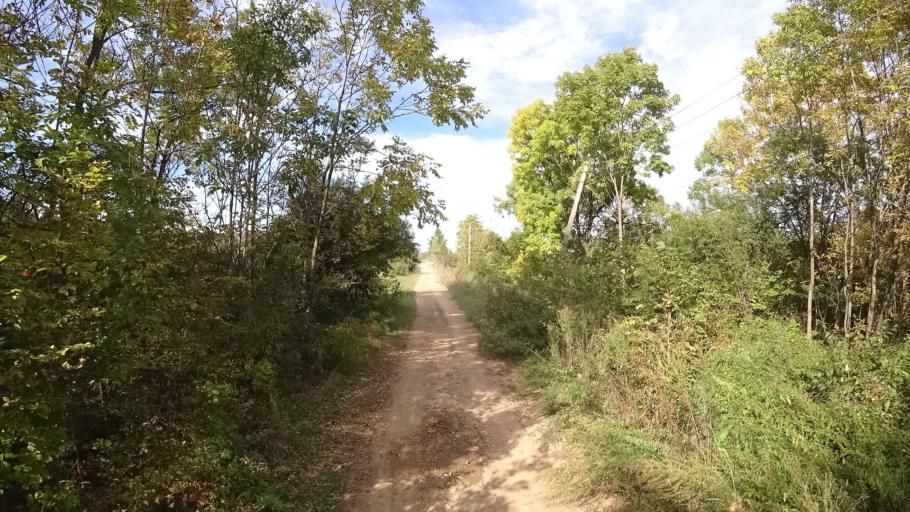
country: RU
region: Primorskiy
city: Dostoyevka
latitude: 44.2943
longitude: 133.4590
